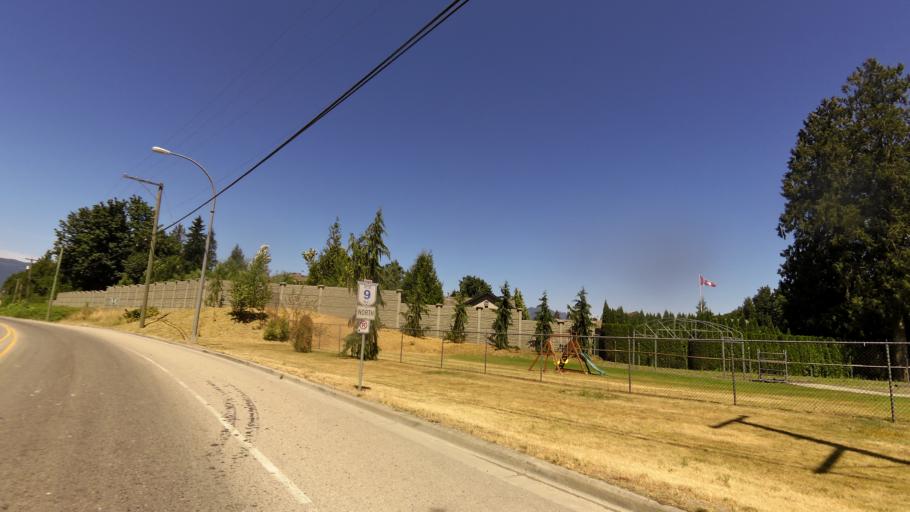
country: CA
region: British Columbia
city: Agassiz
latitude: 49.1856
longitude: -121.7652
